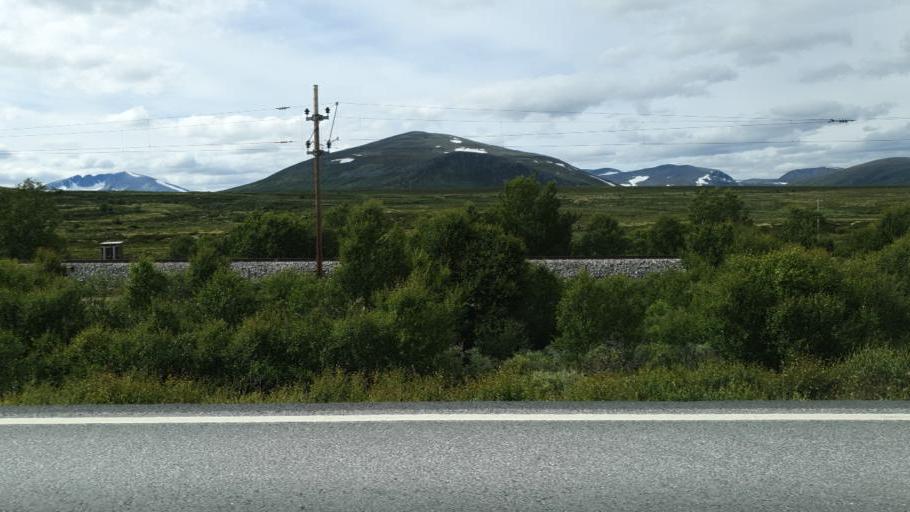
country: NO
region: Sor-Trondelag
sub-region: Oppdal
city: Oppdal
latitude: 62.2567
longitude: 9.5509
